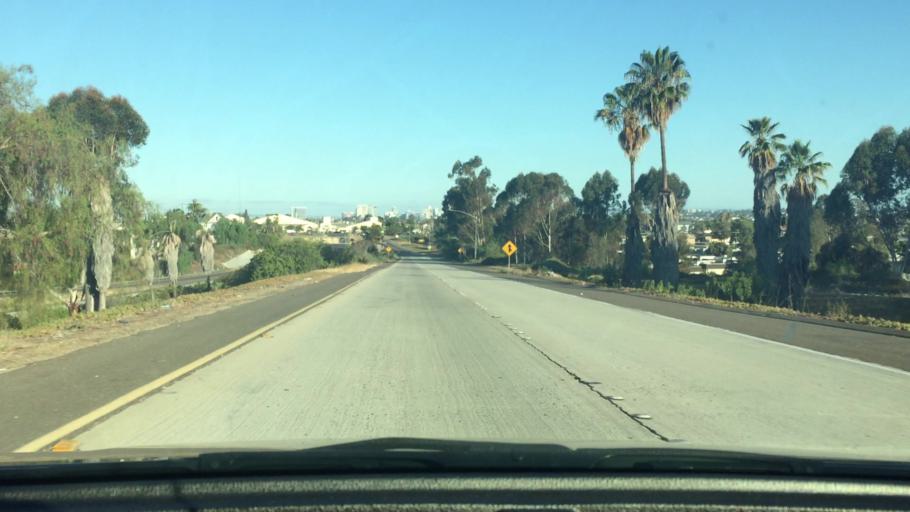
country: US
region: California
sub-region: San Diego County
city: National City
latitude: 32.6902
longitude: -117.0966
